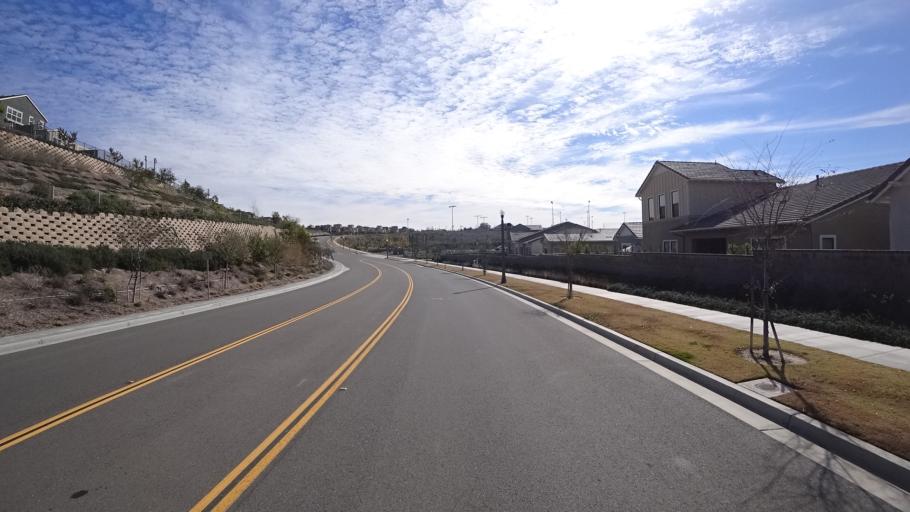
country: US
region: California
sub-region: Orange County
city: Ladera Ranch
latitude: 33.5507
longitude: -117.6026
